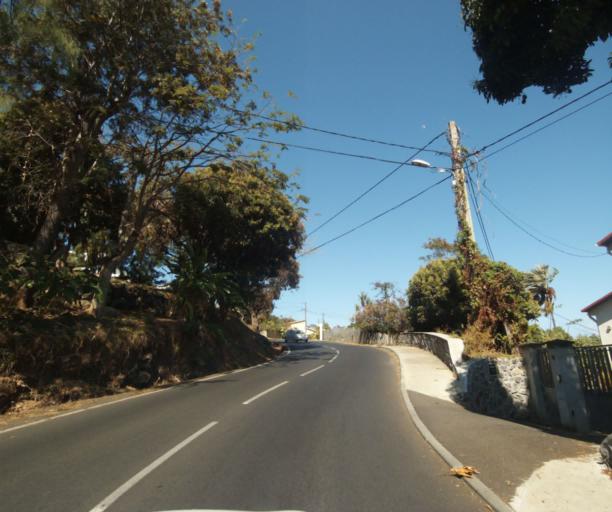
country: RE
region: Reunion
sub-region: Reunion
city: Saint-Paul
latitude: -20.9951
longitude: 55.3302
